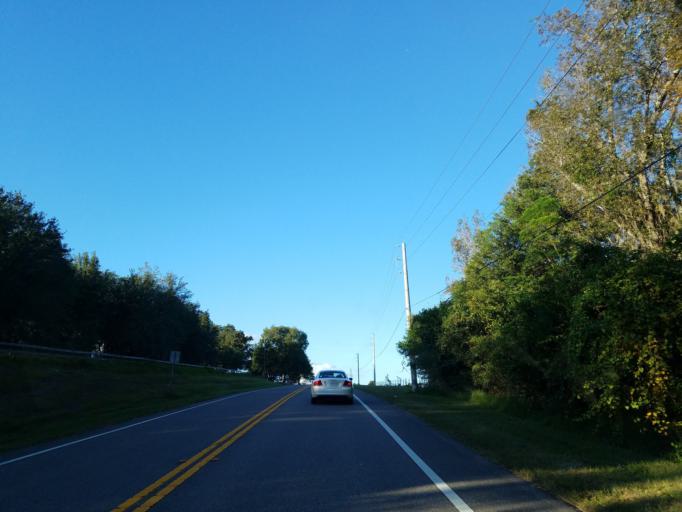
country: US
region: Florida
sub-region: Hernando County
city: Hill 'n Dale
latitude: 28.4820
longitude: -82.3029
